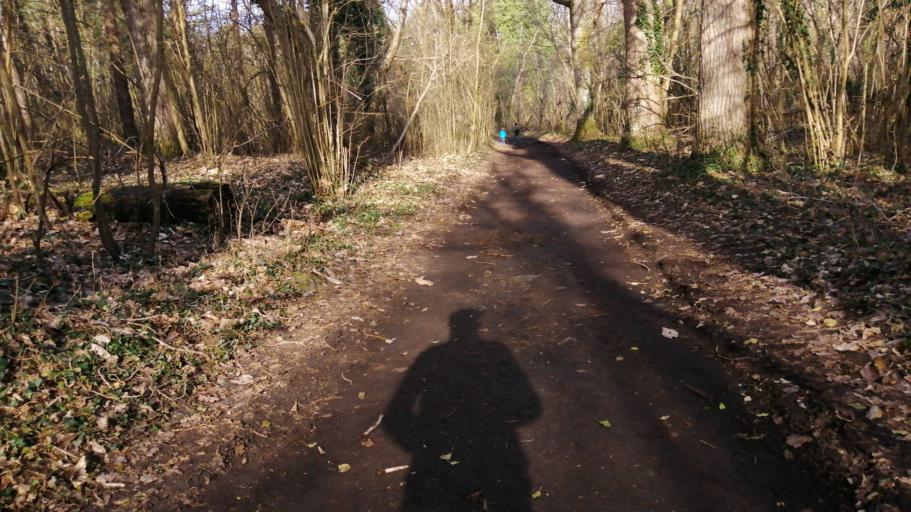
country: FR
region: Nord-Pas-de-Calais
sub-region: Departement du Pas-de-Calais
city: Dannes
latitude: 50.5980
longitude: 1.6088
